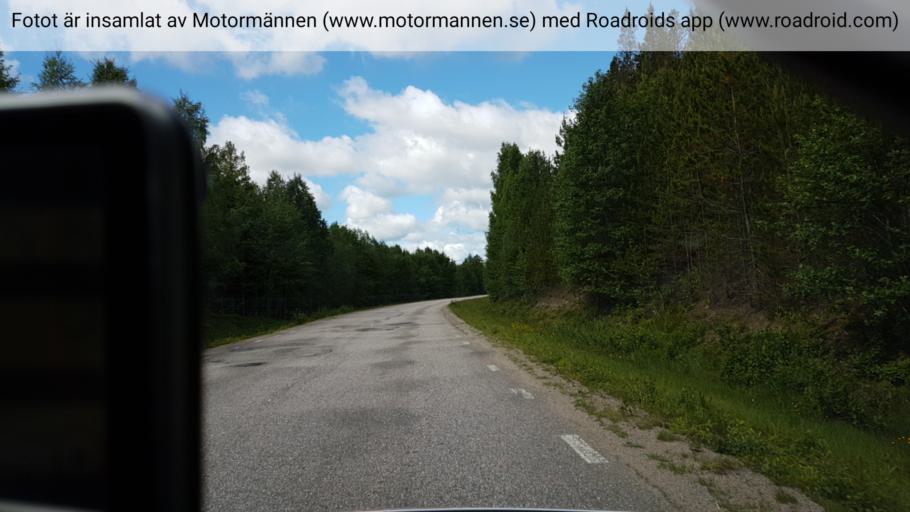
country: SE
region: Gaevleborg
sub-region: Hudiksvalls Kommun
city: Delsbo
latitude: 61.6056
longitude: 16.7227
